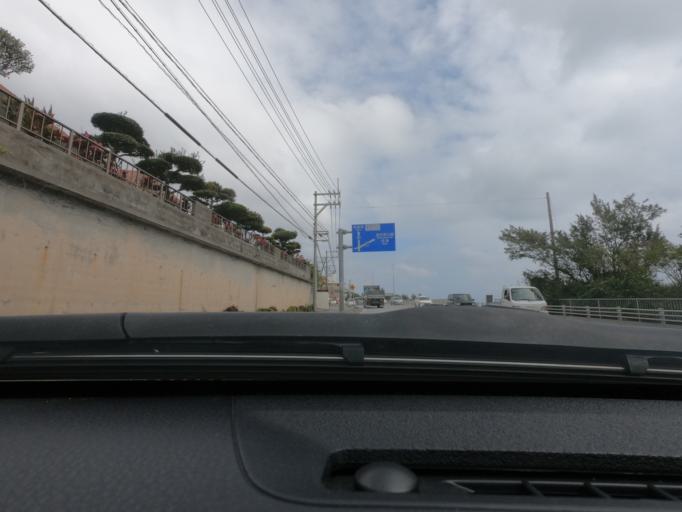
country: JP
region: Okinawa
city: Ishikawa
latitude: 26.4497
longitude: 127.9068
